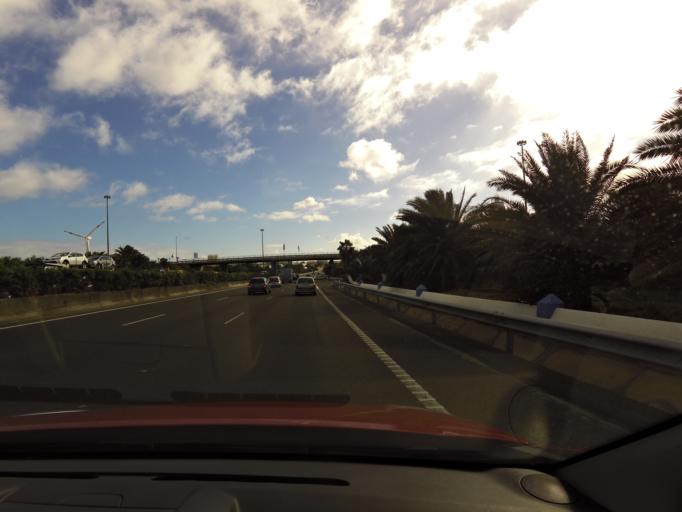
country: ES
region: Canary Islands
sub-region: Provincia de Las Palmas
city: Telde
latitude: 27.9513
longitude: -15.3874
